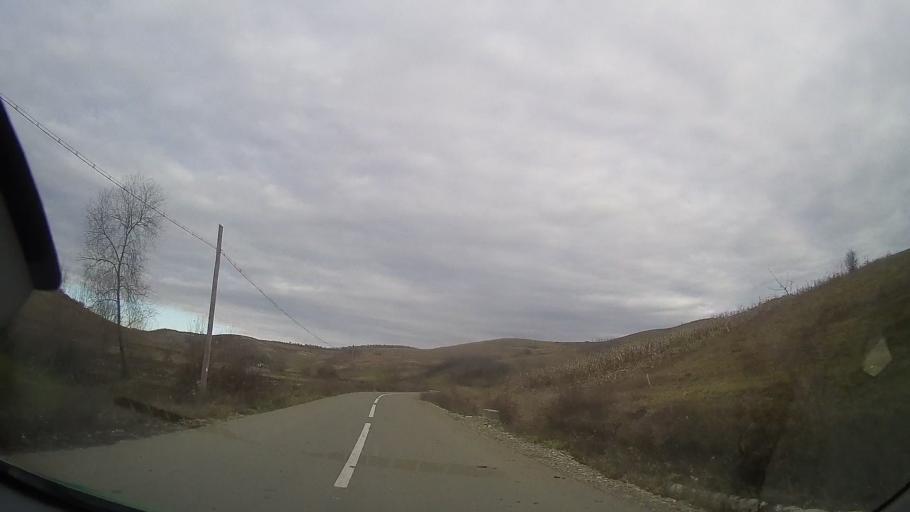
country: RO
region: Bistrita-Nasaud
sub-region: Comuna Silvasu de Campie
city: Silvasu de Campie
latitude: 46.8225
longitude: 24.3017
